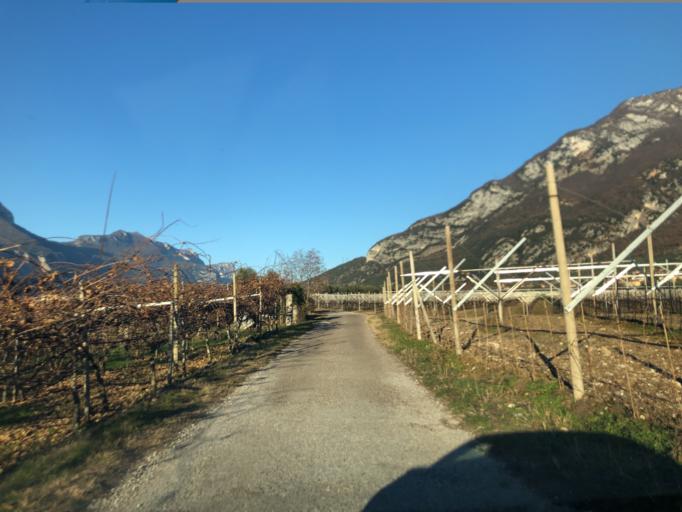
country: IT
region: Trentino-Alto Adige
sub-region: Provincia di Trento
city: Bolognano-Vignole
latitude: 45.9054
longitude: 10.8952
